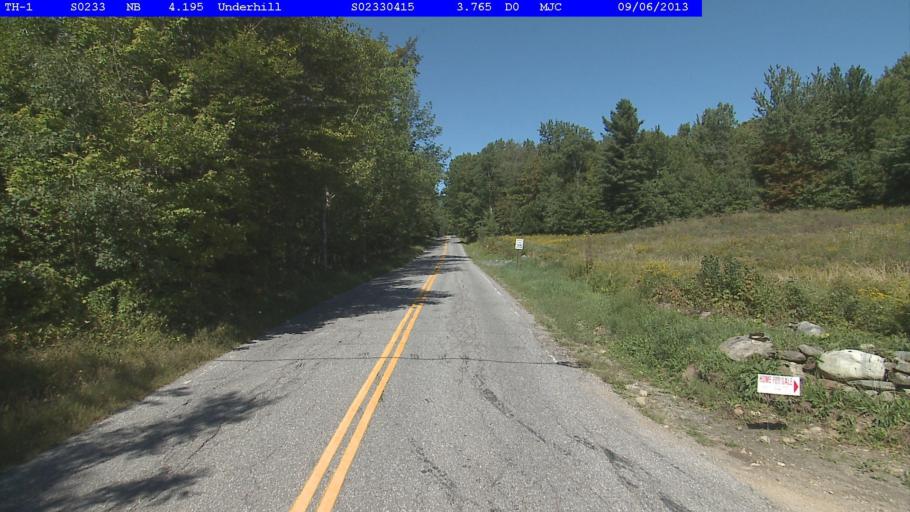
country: US
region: Vermont
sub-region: Chittenden County
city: Jericho
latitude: 44.5214
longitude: -72.8815
